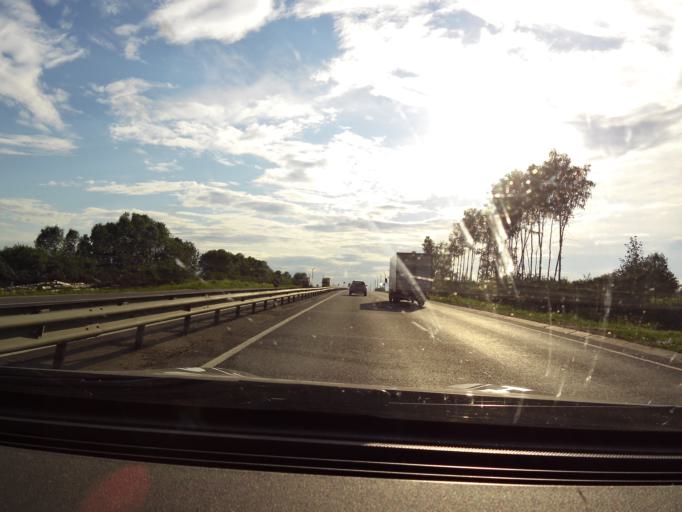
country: RU
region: Vladimir
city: Melekhovo
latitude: 56.2036
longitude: 41.1421
